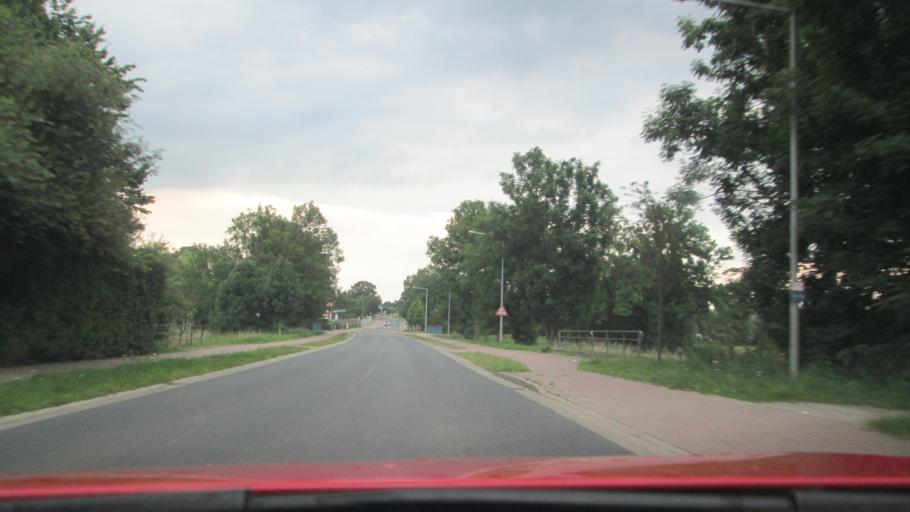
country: DE
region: Lower Saxony
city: Lehre
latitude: 52.3335
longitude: 10.6733
